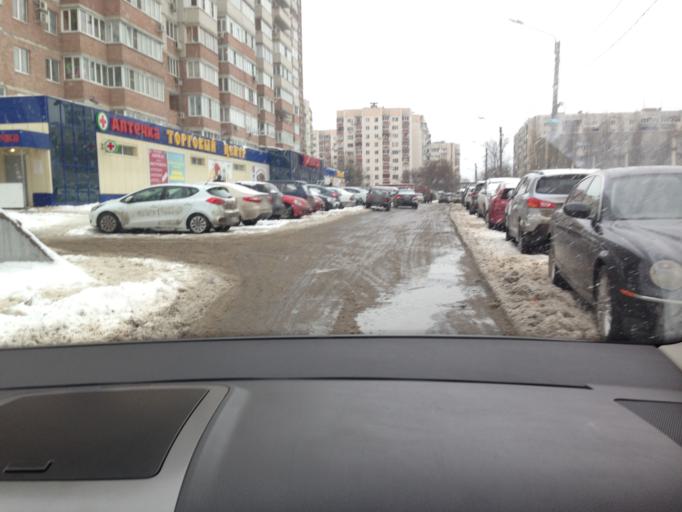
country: RU
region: Voronezj
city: Voronezh
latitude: 51.6699
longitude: 39.1849
